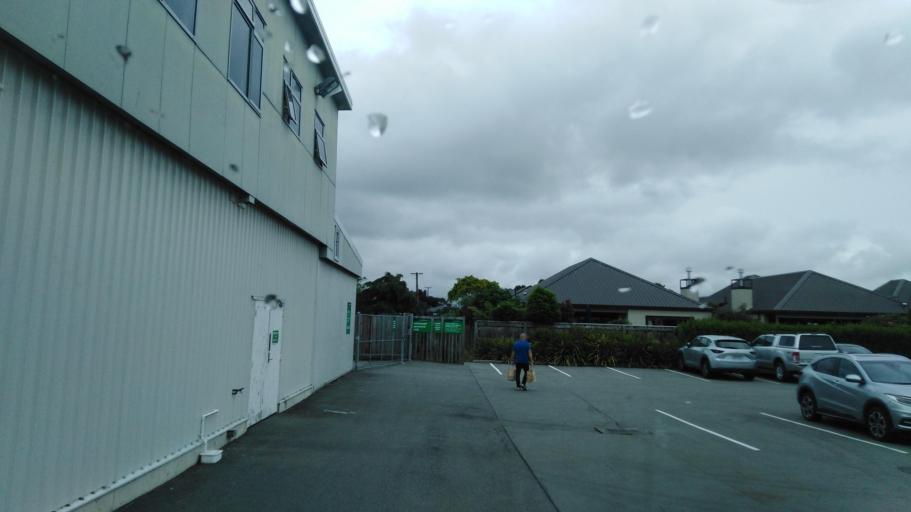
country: NZ
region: Marlborough
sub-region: Marlborough District
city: Blenheim
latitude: -41.5099
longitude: 173.9347
